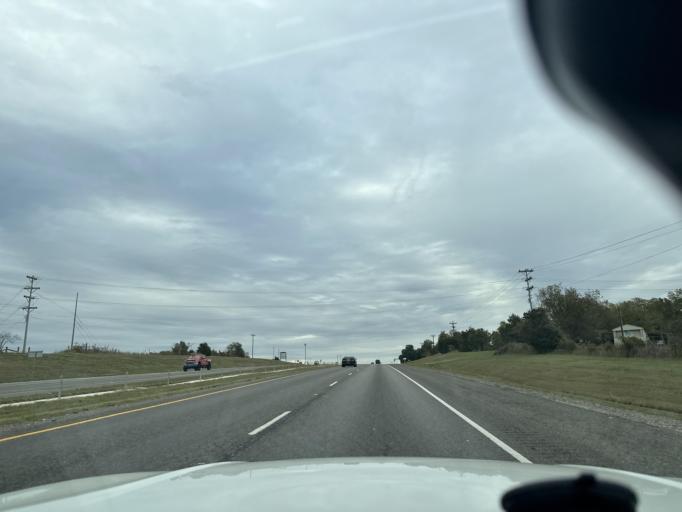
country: US
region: Texas
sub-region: Burleson County
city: Somerville
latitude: 30.1840
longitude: -96.5827
